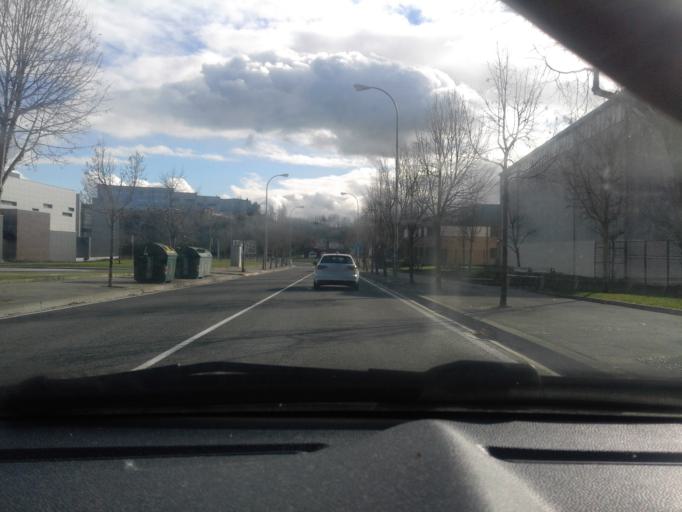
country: ES
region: Navarre
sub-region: Provincia de Navarra
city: Burlata
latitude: 42.8263
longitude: -1.6113
